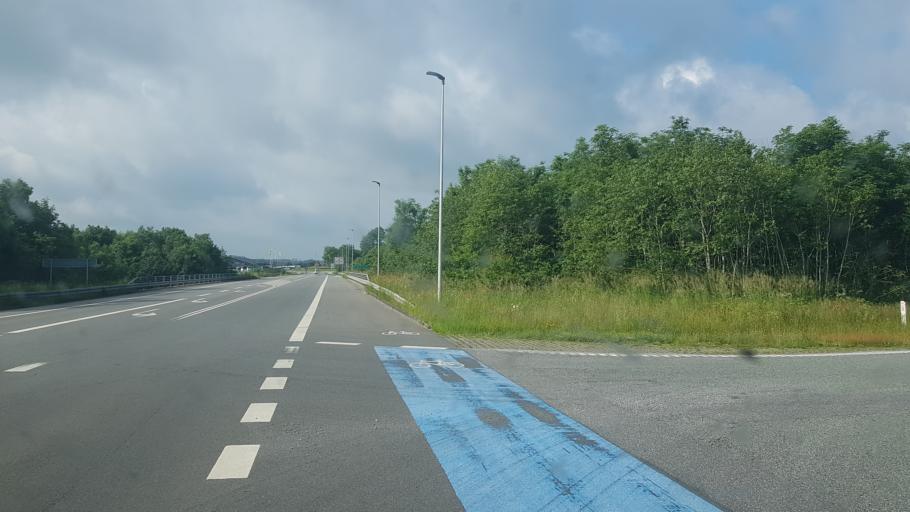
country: DK
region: South Denmark
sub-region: Vejen Kommune
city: Brorup
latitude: 55.5051
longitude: 9.0214
